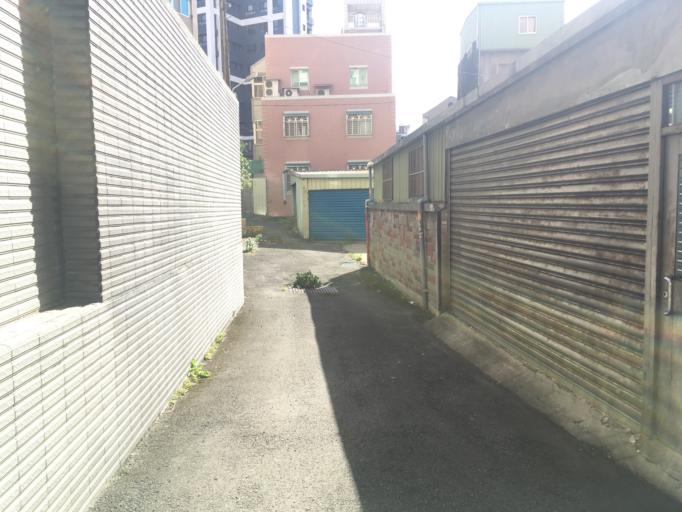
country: TW
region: Taiwan
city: Daxi
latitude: 24.9019
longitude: 121.1480
